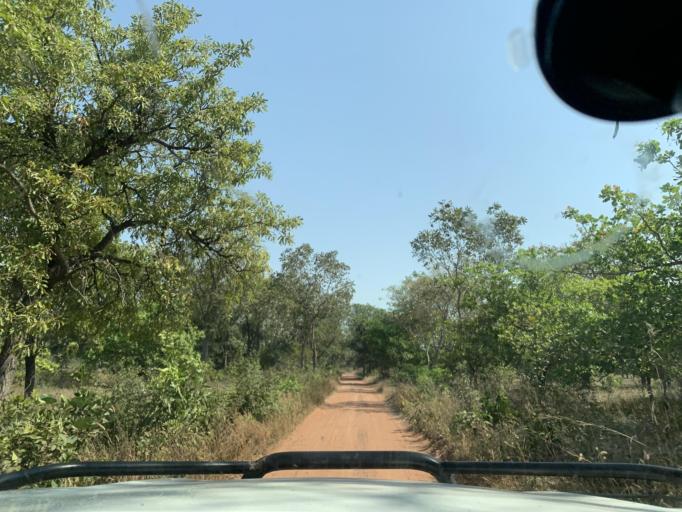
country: ML
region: Sikasso
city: Kolondieba
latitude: 10.8922
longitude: -6.7518
